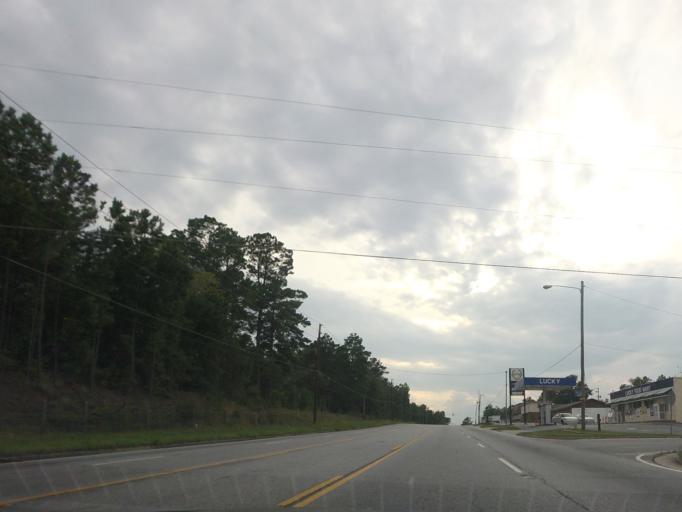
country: US
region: Georgia
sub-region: Bibb County
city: Macon
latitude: 32.8419
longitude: -83.5620
